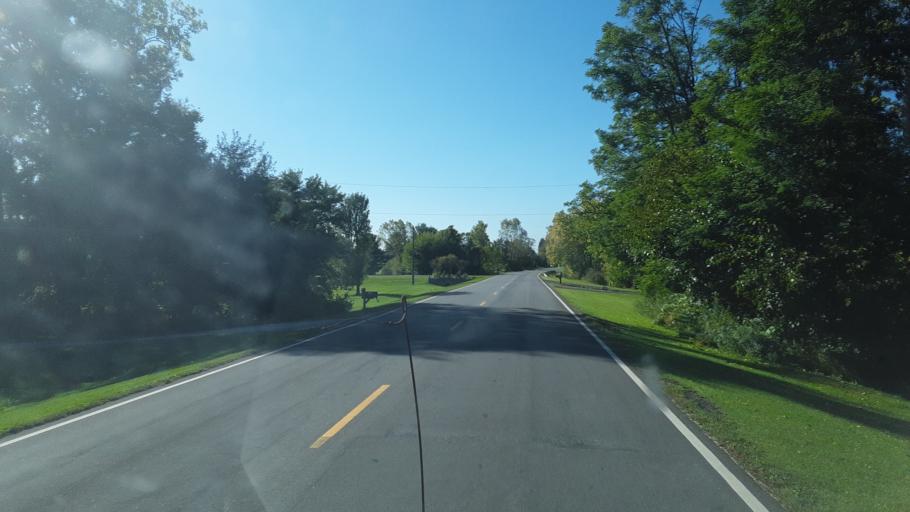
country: US
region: Ohio
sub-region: Delaware County
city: Sunbury
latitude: 40.2407
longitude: -82.7893
